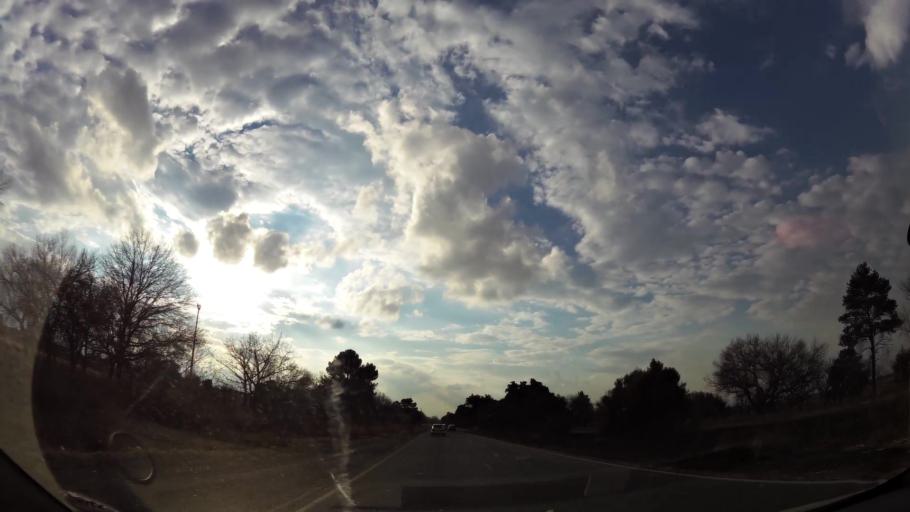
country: ZA
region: Orange Free State
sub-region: Fezile Dabi District Municipality
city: Sasolburg
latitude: -26.7939
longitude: 27.8286
